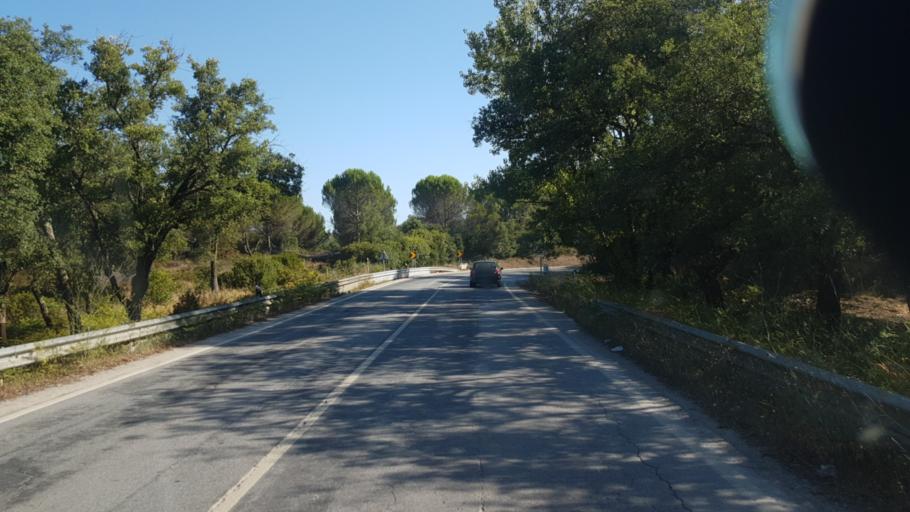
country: PT
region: Setubal
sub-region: Sesimbra
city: Sesimbra
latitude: 38.4803
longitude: -9.0735
